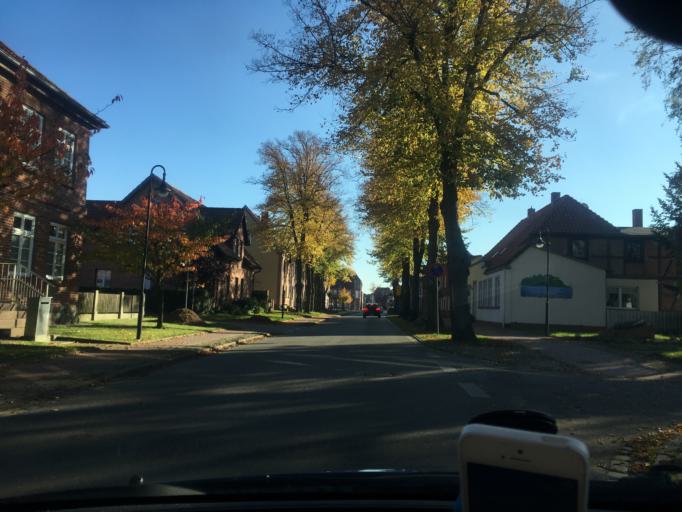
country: DE
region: Mecklenburg-Vorpommern
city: Zarrentin
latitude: 53.5545
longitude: 10.9152
